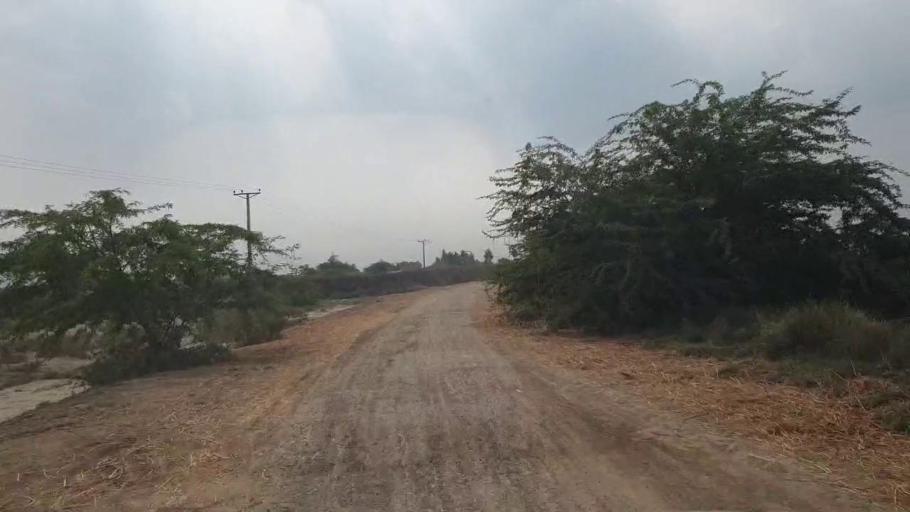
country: PK
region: Sindh
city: Talhar
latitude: 24.9319
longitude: 68.7880
